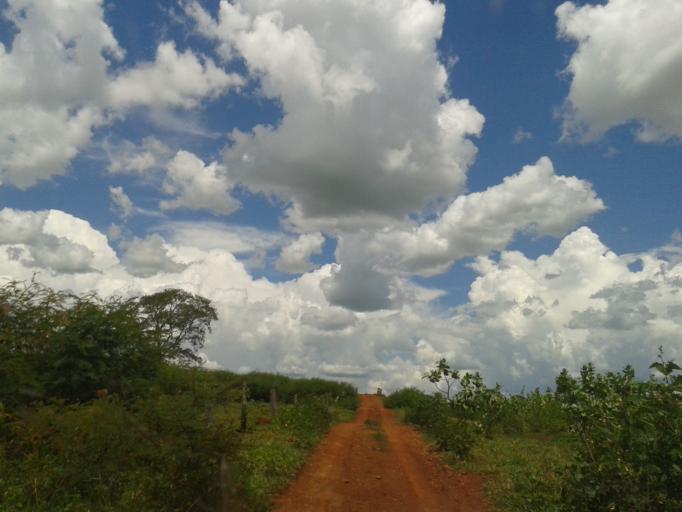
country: BR
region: Minas Gerais
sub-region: Capinopolis
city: Capinopolis
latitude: -18.7856
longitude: -49.8110
